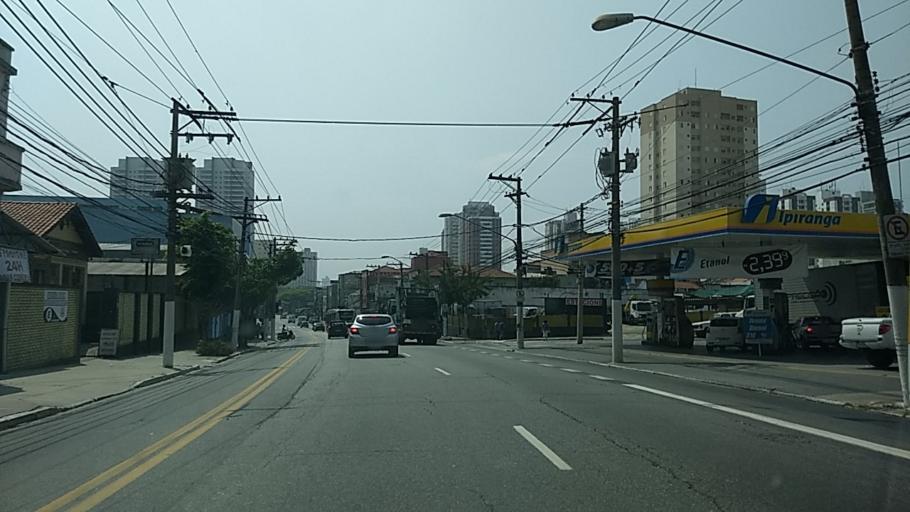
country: BR
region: Sao Paulo
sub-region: Sao Paulo
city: Sao Paulo
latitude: -23.5357
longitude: -46.5710
